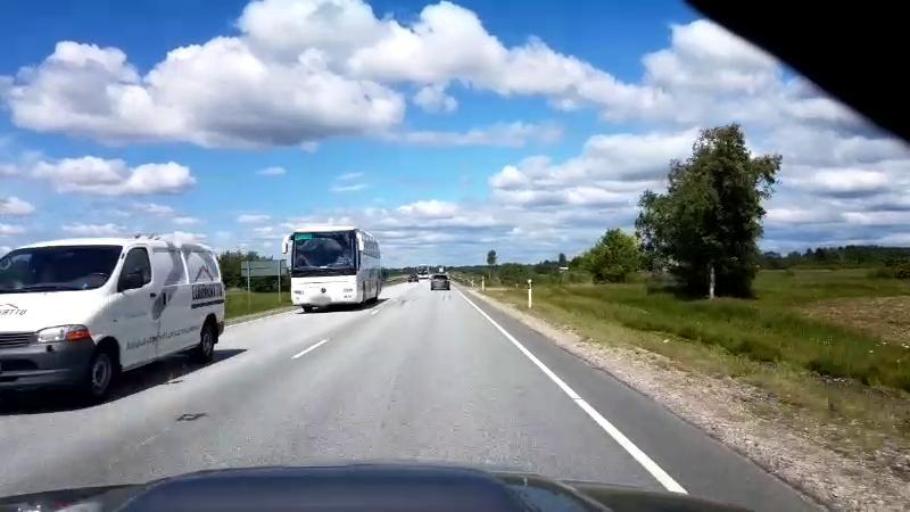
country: EE
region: Paernumaa
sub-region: Sauga vald
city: Sauga
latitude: 58.4800
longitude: 24.5279
